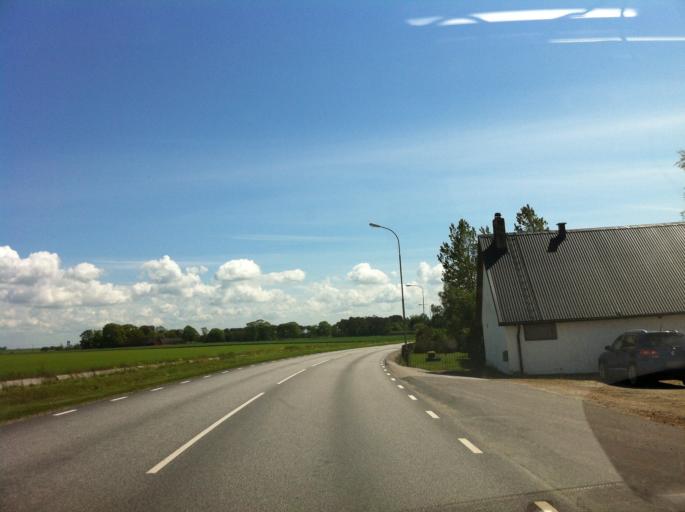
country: SE
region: Skane
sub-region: Kavlinge Kommun
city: Loddekopinge
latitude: 55.7864
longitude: 13.0041
